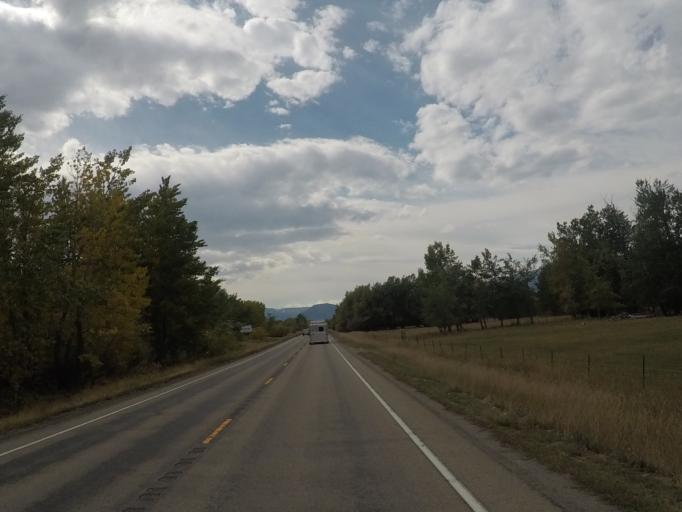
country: US
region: Montana
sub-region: Carbon County
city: Red Lodge
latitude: 45.2720
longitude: -109.2205
